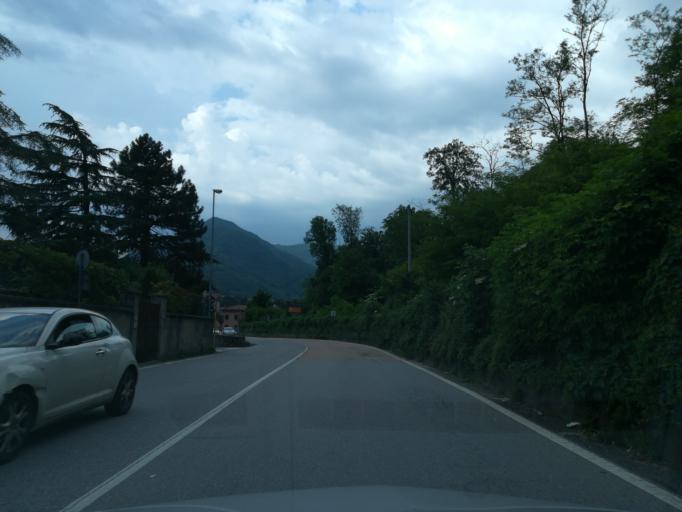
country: IT
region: Lombardy
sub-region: Provincia di Bergamo
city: Villa d'Alme
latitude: 45.7463
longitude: 9.6094
